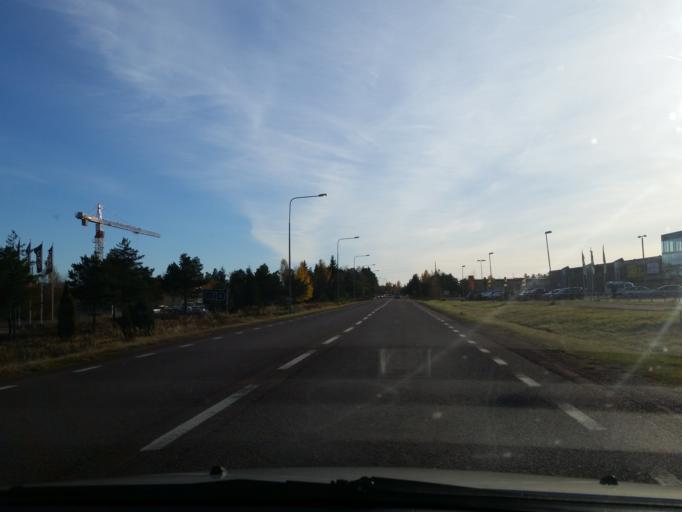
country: AX
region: Alands landsbygd
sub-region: Jomala
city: Jomala
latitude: 60.1309
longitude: 19.9349
